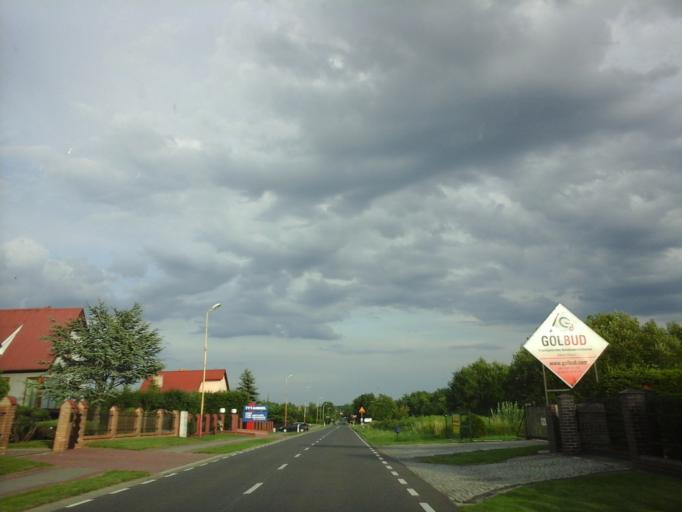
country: PL
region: West Pomeranian Voivodeship
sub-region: Powiat kamienski
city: Golczewo
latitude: 53.8320
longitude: 14.9650
